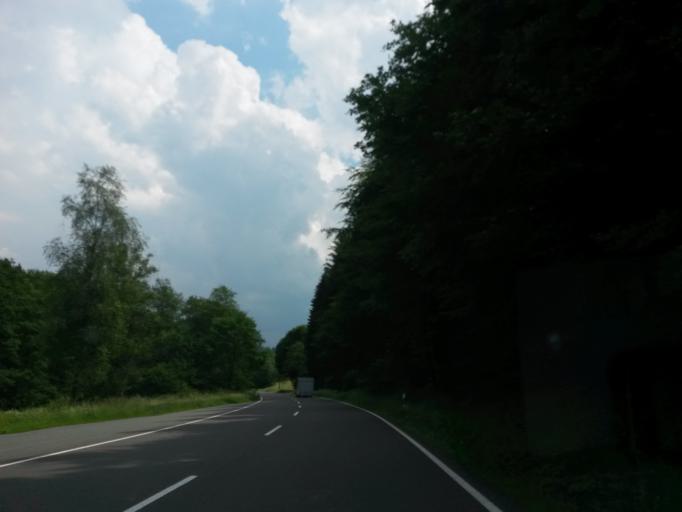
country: DE
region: North Rhine-Westphalia
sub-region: Regierungsbezirk Arnsberg
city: Olpe
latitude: 51.0271
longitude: 7.8939
